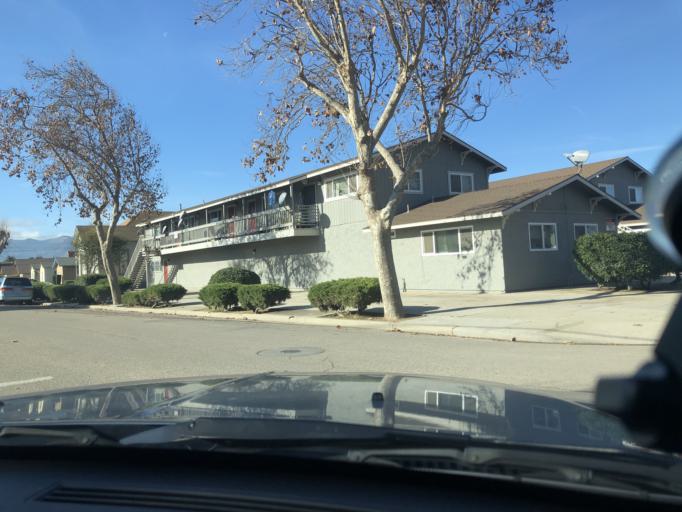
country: US
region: California
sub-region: Monterey County
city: King City
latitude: 36.2099
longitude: -121.1297
